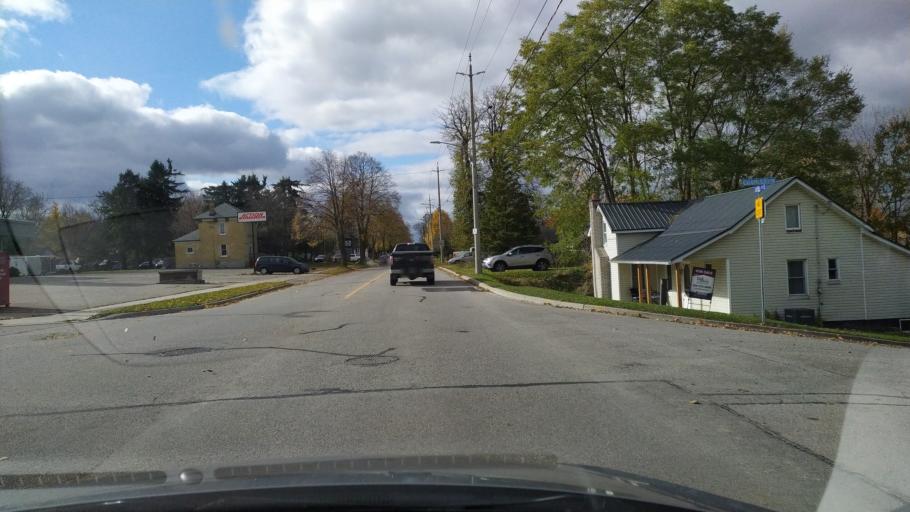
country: CA
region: Ontario
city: Stratford
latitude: 43.2613
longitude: -81.1255
